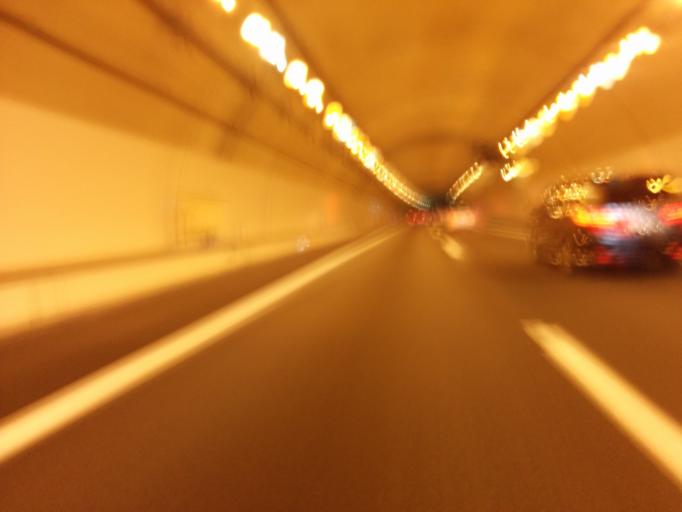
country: JP
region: Shiga Prefecture
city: Kusatsu
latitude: 34.9615
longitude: 135.9993
